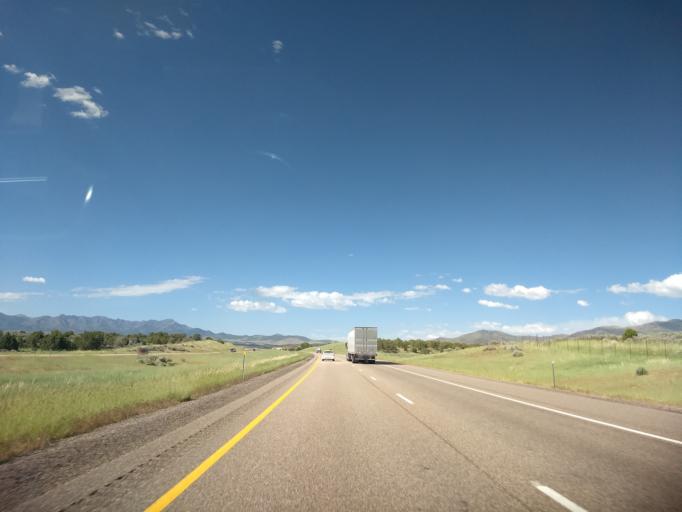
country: US
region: Utah
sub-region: Millard County
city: Fillmore
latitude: 39.0980
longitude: -112.2605
